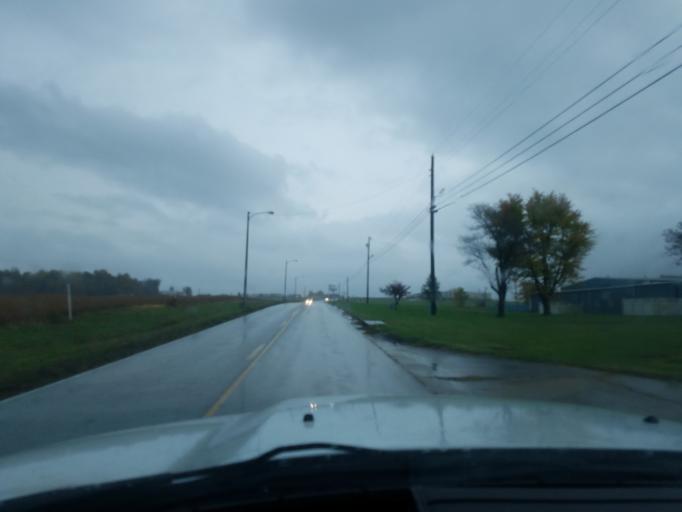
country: US
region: Kentucky
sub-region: Taylor County
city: Campbellsville
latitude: 37.3472
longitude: -85.3279
